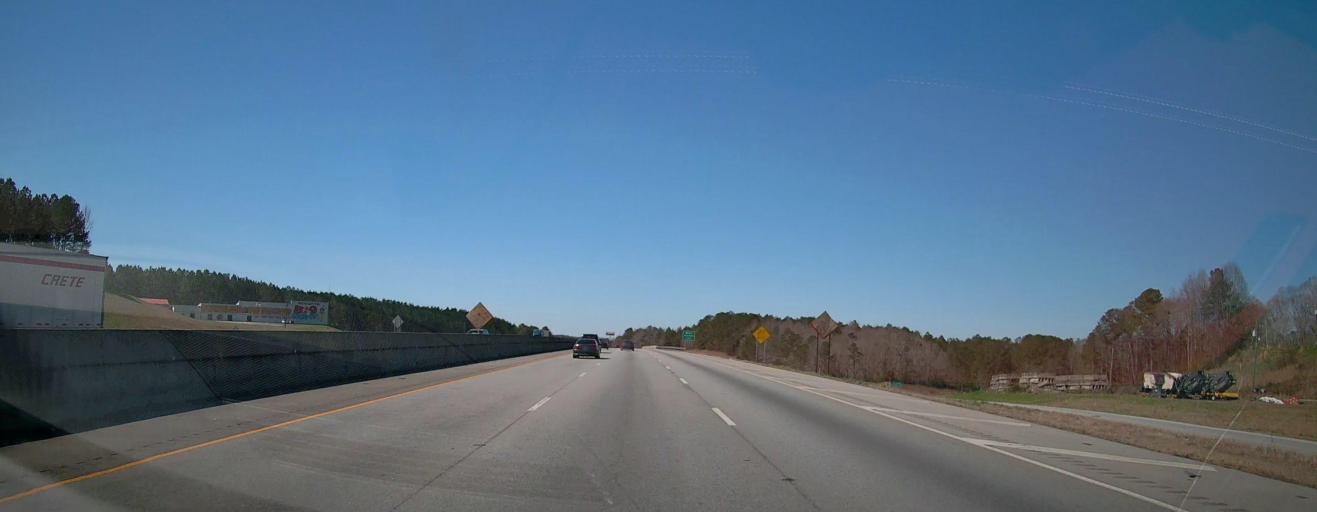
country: US
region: Georgia
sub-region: Haralson County
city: Tallapoosa
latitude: 33.6547
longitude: -85.4116
